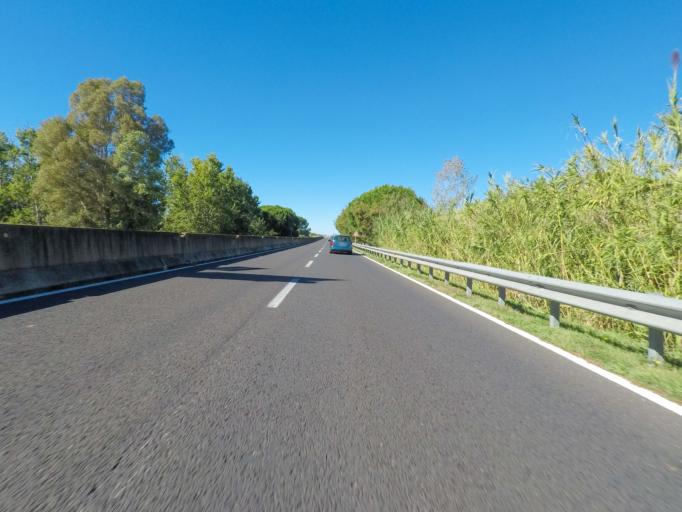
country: IT
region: Tuscany
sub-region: Provincia di Grosseto
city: Orbetello Scalo
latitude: 42.4751
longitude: 11.2330
